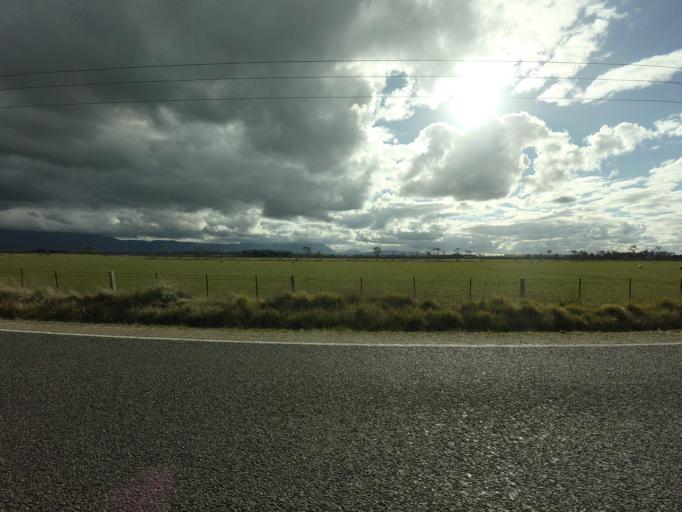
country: AU
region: Tasmania
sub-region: Northern Midlands
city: Longford
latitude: -41.7374
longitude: 147.0839
